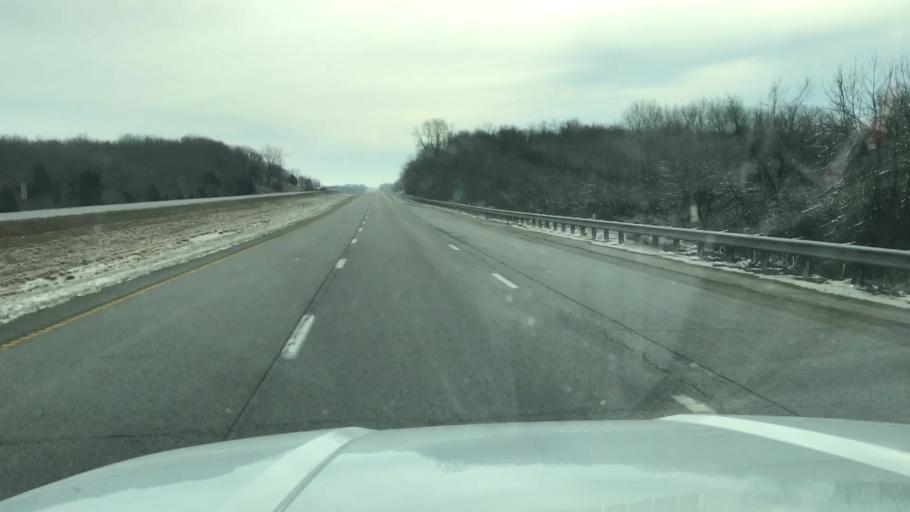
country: US
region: Missouri
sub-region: Andrew County
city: Savannah
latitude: 39.9114
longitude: -94.8975
